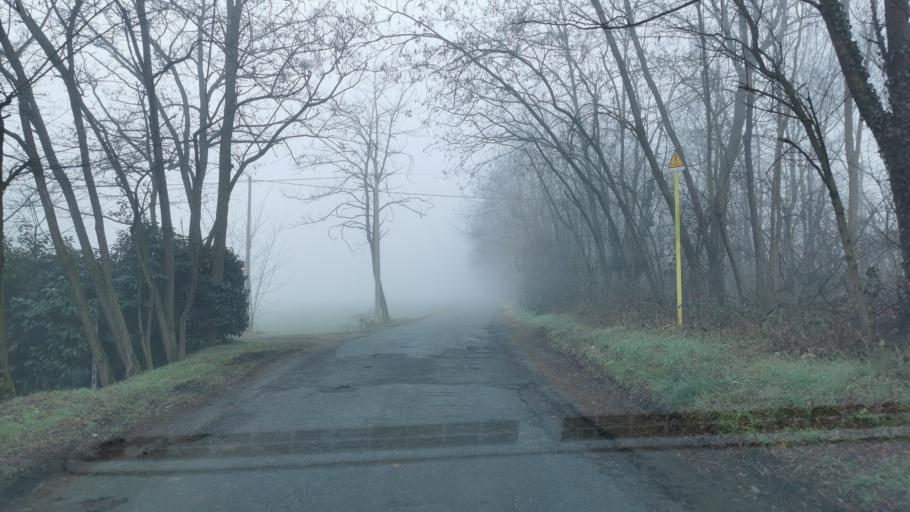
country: IT
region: Piedmont
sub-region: Provincia di Torino
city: Leini
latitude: 45.1886
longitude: 7.7401
